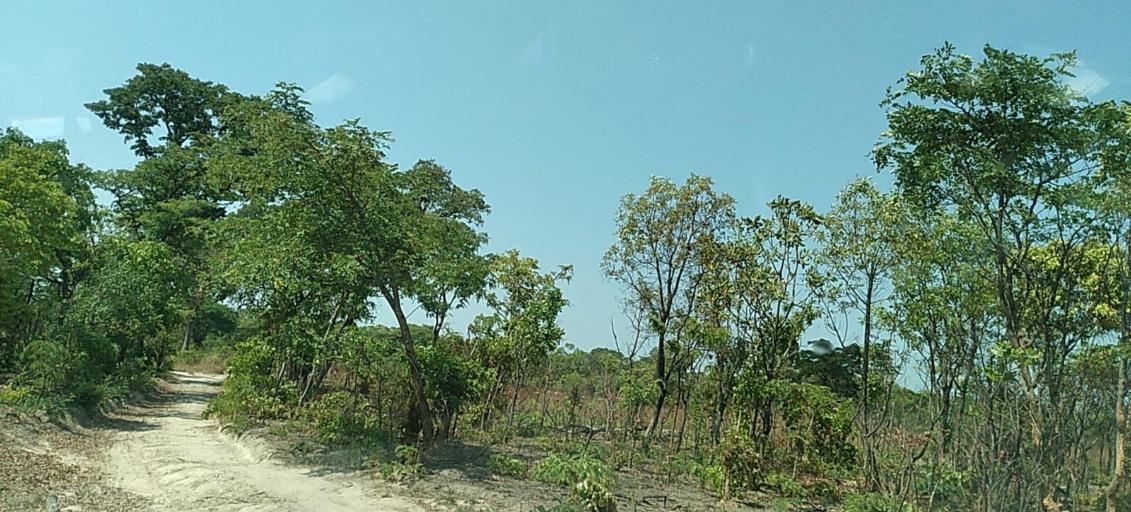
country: ZM
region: Copperbelt
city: Mpongwe
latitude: -13.7771
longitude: 28.1074
